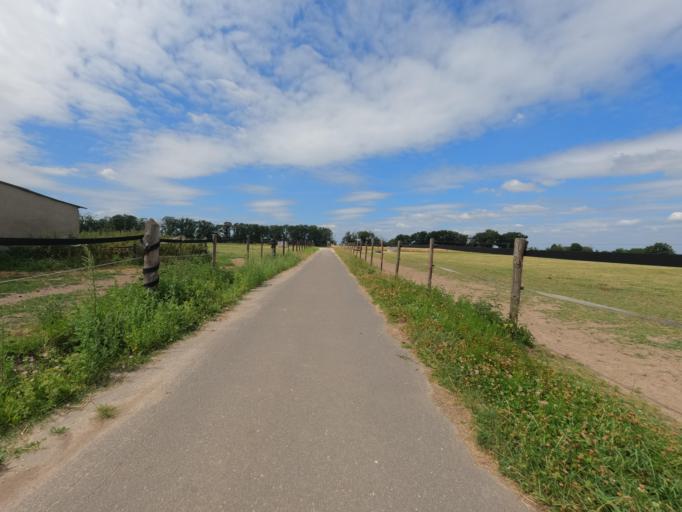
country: DE
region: North Rhine-Westphalia
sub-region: Regierungsbezirk Koln
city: Heinsberg
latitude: 51.0514
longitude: 6.1218
